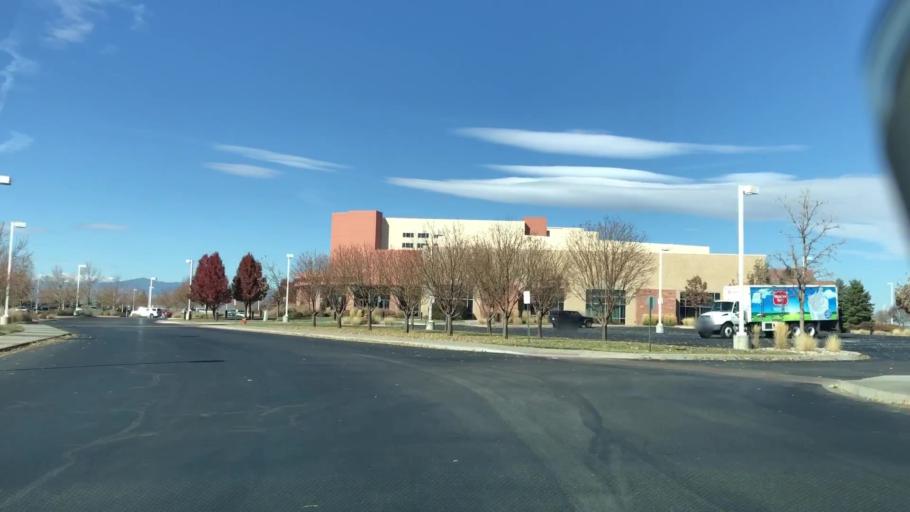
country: US
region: Colorado
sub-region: Weld County
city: Windsor
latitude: 40.4398
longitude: -104.9882
